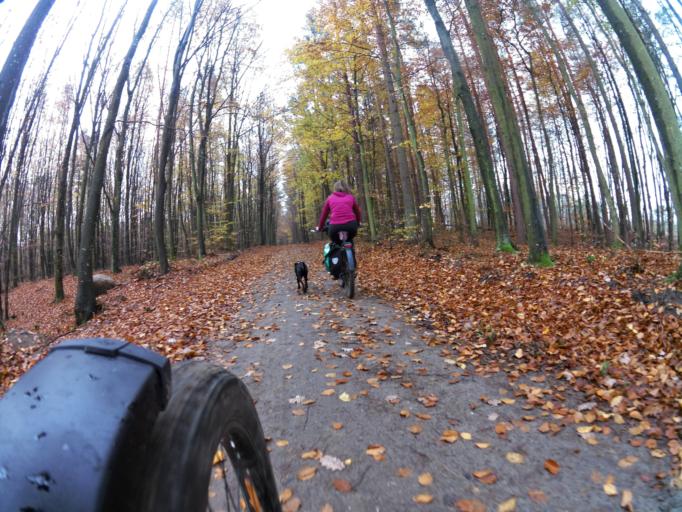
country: PL
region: Pomeranian Voivodeship
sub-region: Powiat pucki
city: Krokowa
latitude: 54.7748
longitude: 18.0915
